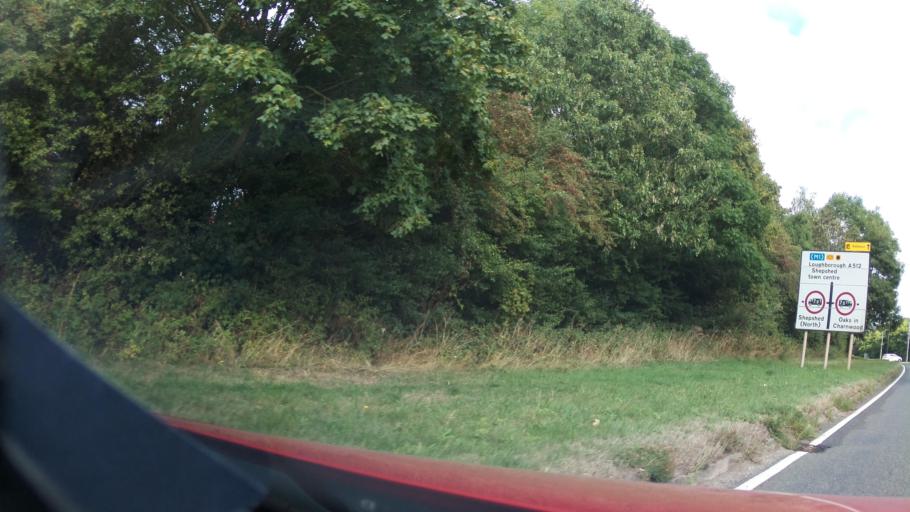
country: GB
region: England
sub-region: Leicestershire
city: Shepshed
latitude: 52.7608
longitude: -1.3182
